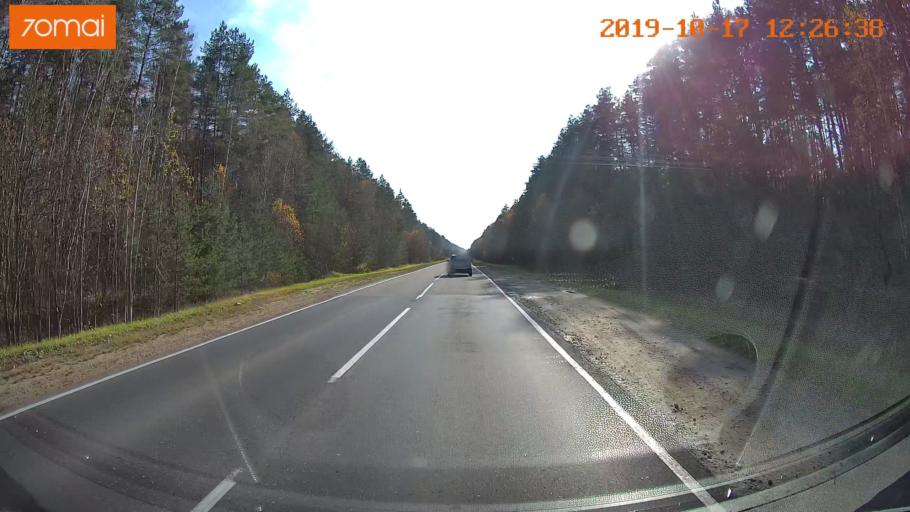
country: RU
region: Rjazan
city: Syntul
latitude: 55.0165
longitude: 41.2574
